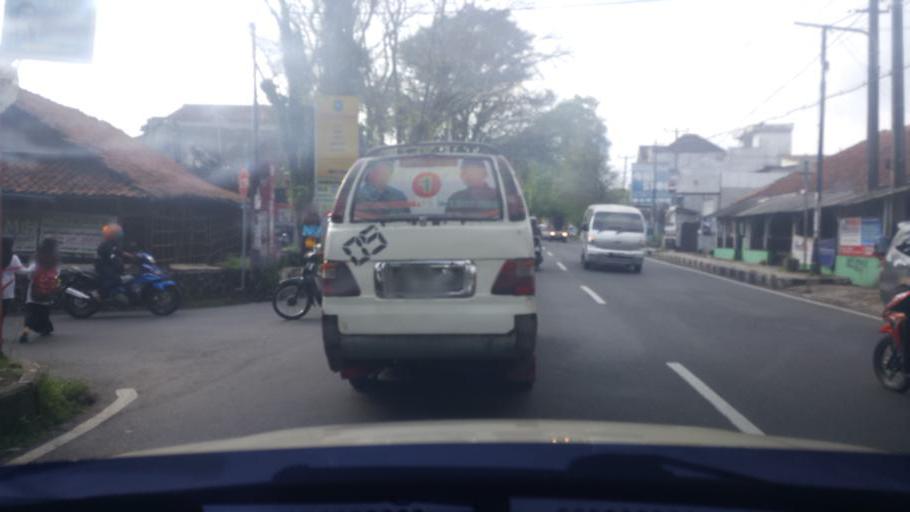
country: ID
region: West Java
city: Mancogeh
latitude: -7.3142
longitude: 108.2132
